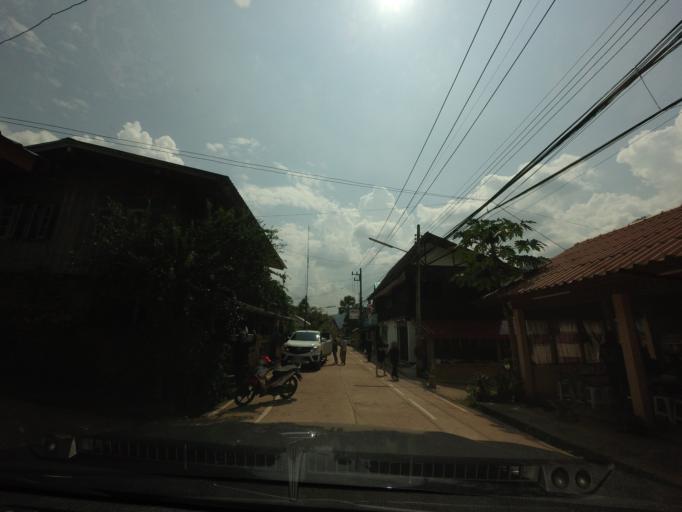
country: TH
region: Nan
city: Bo Kluea
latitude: 19.1501
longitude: 101.1552
